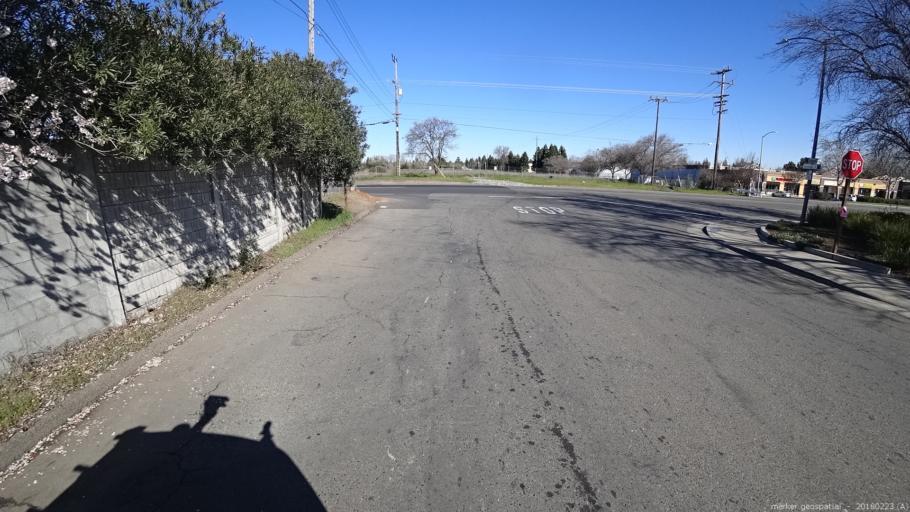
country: US
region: California
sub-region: Sacramento County
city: North Highlands
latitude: 38.7141
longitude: -121.3954
